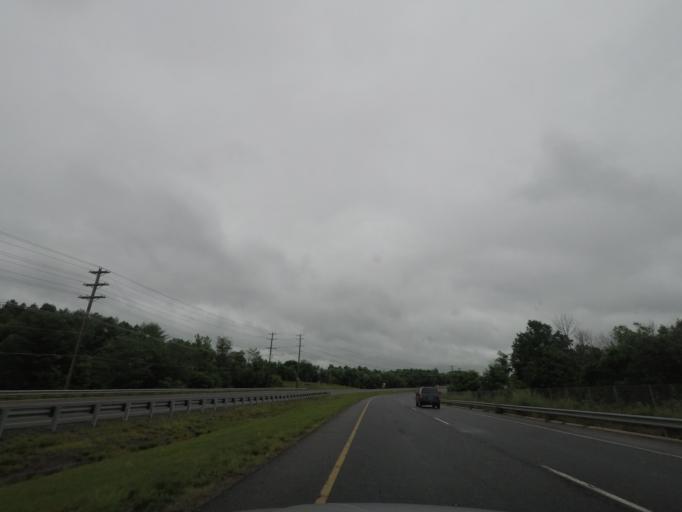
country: US
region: Virginia
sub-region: Prince William County
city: Haymarket
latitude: 38.8501
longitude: -77.6378
